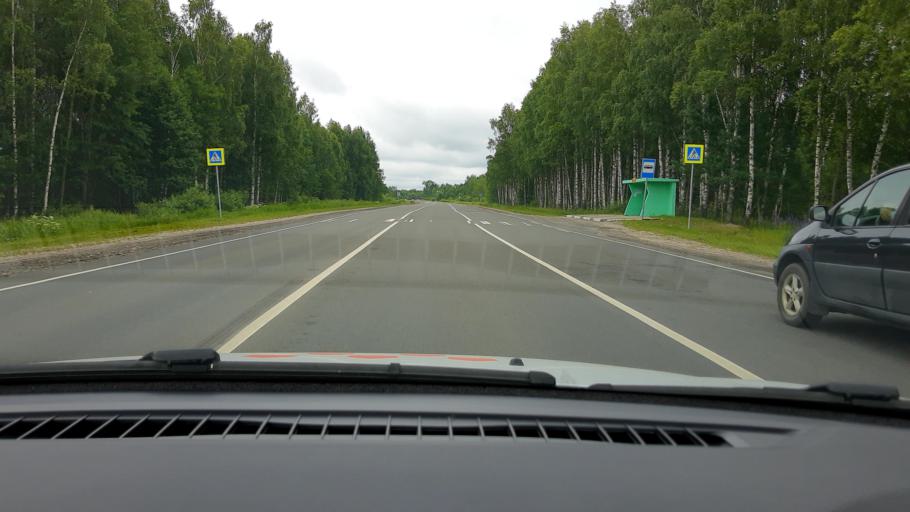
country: RU
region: Nizjnij Novgorod
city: Linda
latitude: 56.5839
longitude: 44.0276
